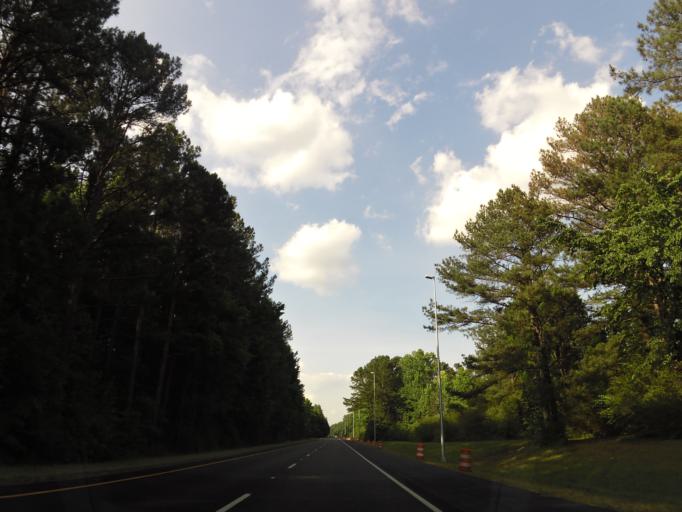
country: US
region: Alabama
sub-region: Jefferson County
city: Trussville
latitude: 33.6097
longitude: -86.6424
